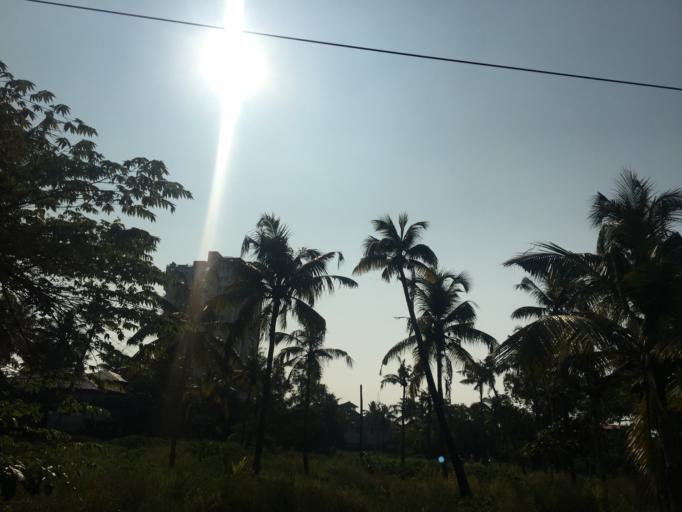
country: IN
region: Kerala
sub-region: Ernakulam
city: Cochin
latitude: 9.9518
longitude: 76.3113
